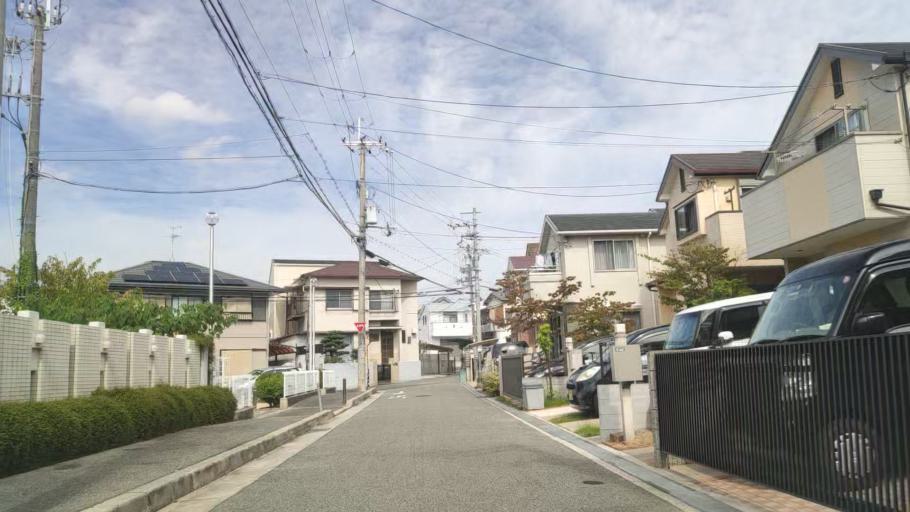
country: JP
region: Osaka
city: Mino
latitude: 34.8134
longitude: 135.4649
